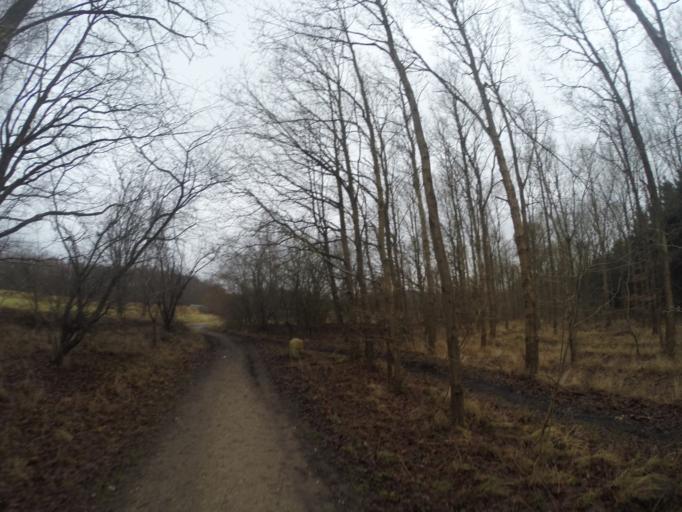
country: DK
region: Capital Region
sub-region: Albertslund Kommune
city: Albertslund
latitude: 55.6841
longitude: 12.3305
